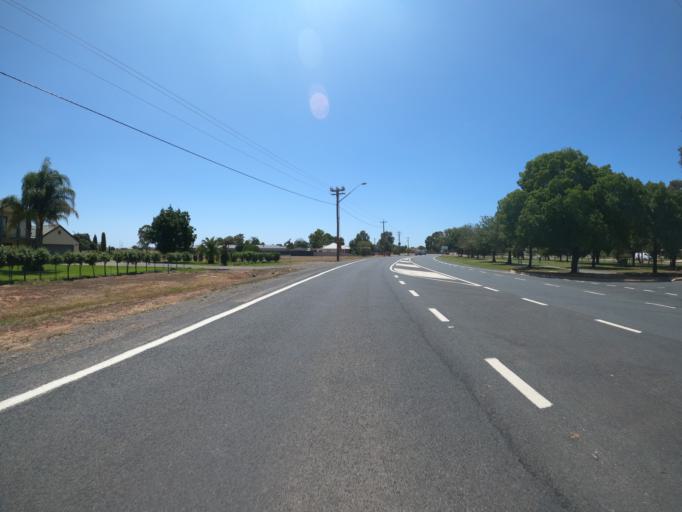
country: AU
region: New South Wales
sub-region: Corowa Shire
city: Mulwala
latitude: -35.9823
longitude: 146.0123
